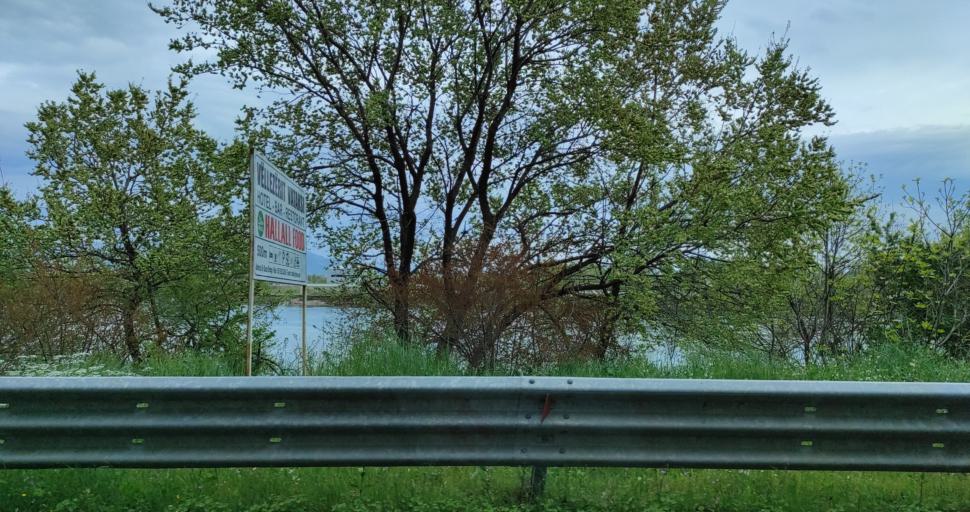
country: AL
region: Shkoder
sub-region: Rrethi i Shkodres
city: Berdica e Madhe
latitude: 42.0419
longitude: 19.4825
